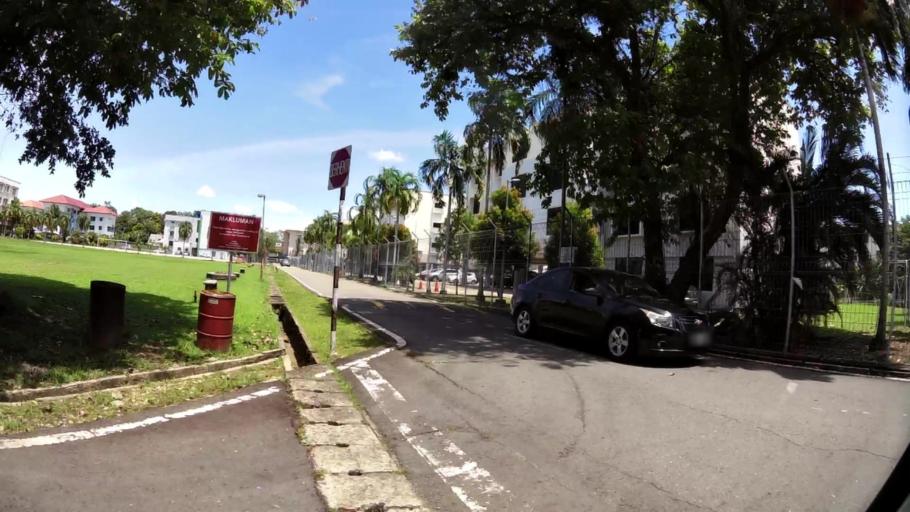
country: BN
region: Brunei and Muara
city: Bandar Seri Begawan
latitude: 4.9351
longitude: 114.9436
